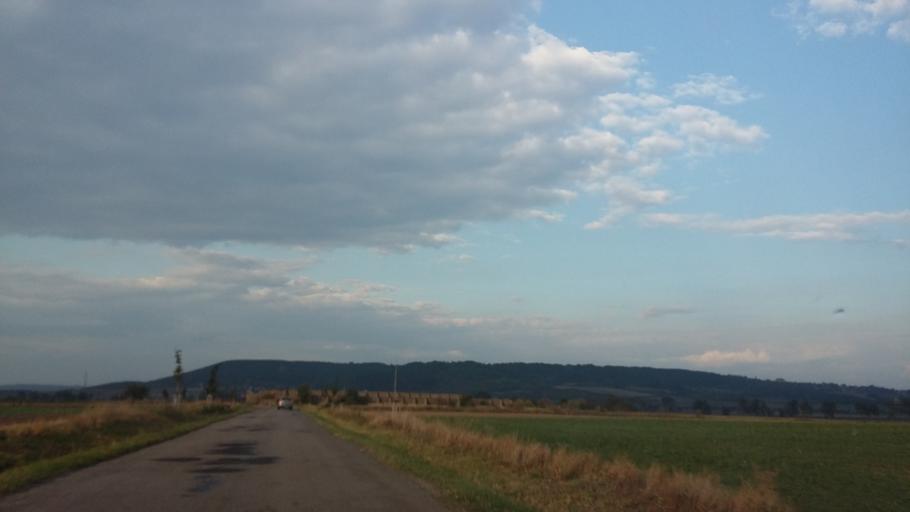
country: CZ
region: Central Bohemia
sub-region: Okres Mlada Boleslav
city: Mlada Boleslav
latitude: 50.3602
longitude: 14.8964
